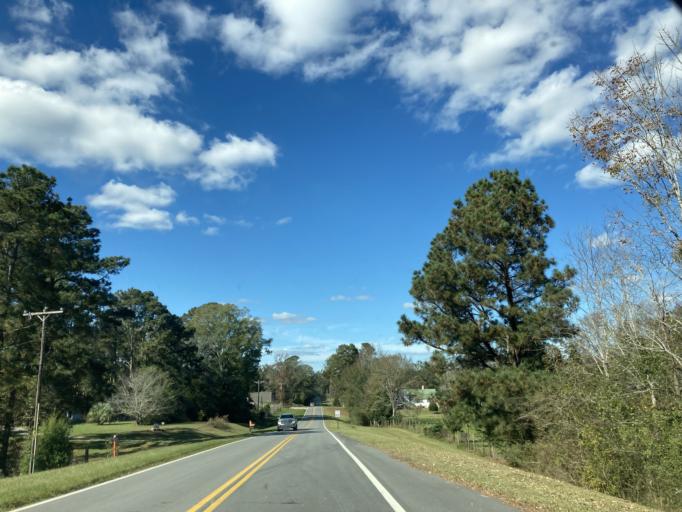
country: US
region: Georgia
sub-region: Jones County
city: Gray
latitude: 32.9379
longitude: -83.5082
